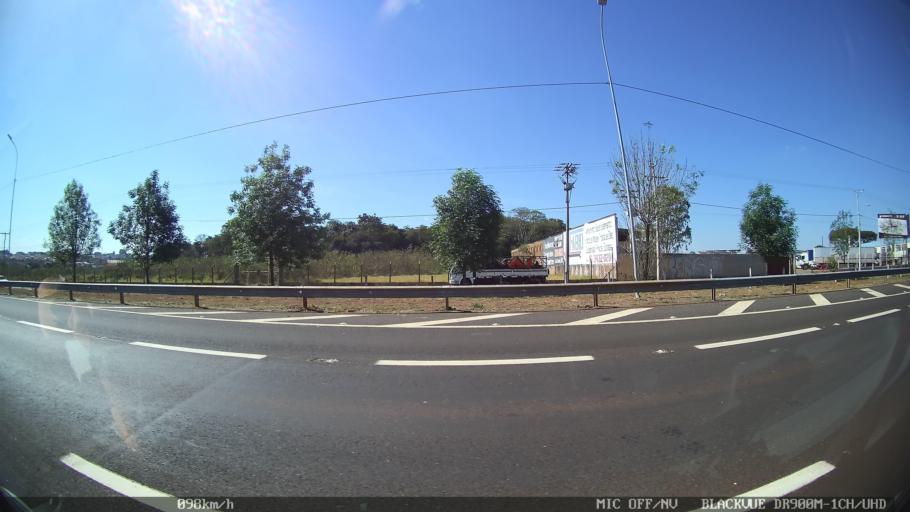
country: BR
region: Sao Paulo
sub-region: Franca
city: Franca
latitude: -20.4946
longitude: -47.4068
